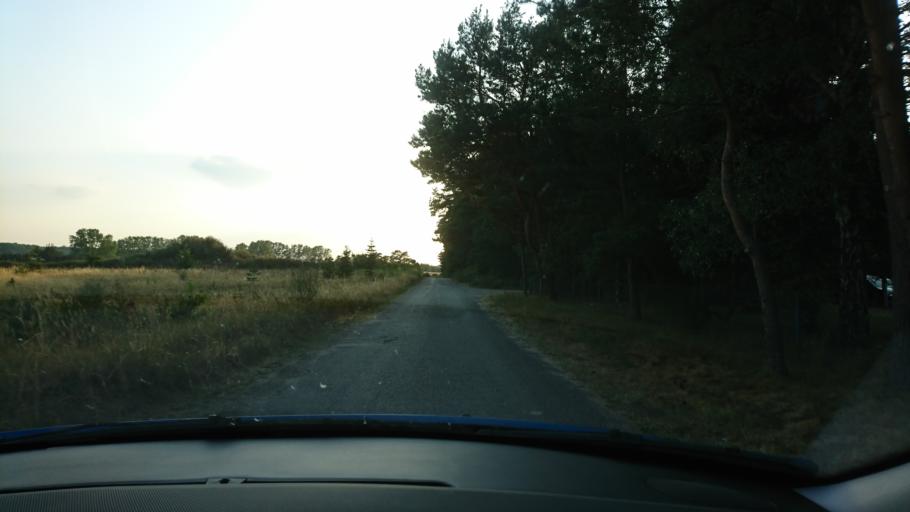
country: SE
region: Skane
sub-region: Simrishamns Kommun
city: Kivik
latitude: 55.7127
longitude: 14.1676
